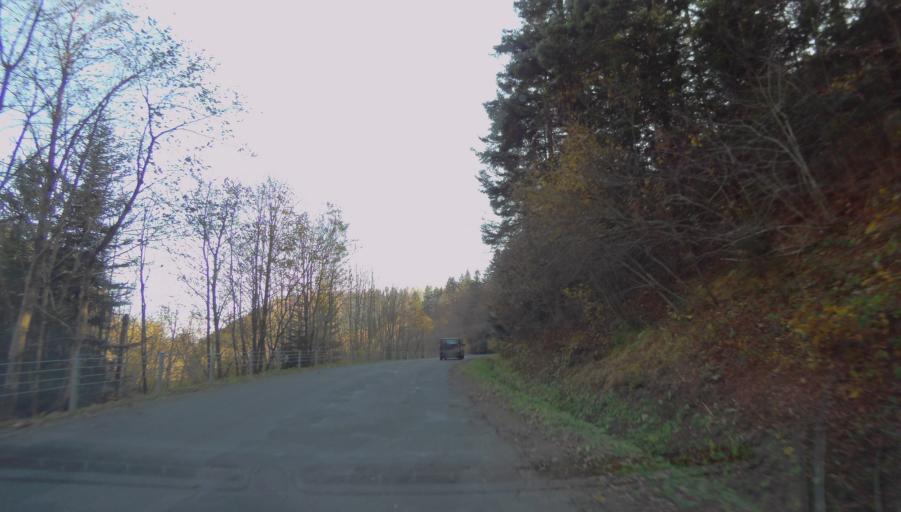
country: PL
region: Subcarpathian Voivodeship
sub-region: Powiat leski
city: Cisna
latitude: 49.2041
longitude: 22.3006
